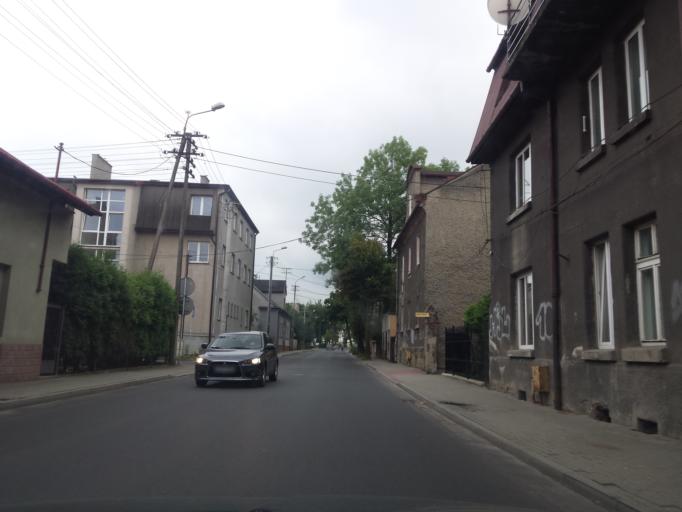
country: PL
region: Silesian Voivodeship
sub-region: Bielsko-Biala
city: Bielsko-Biala
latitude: 49.8146
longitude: 19.0470
